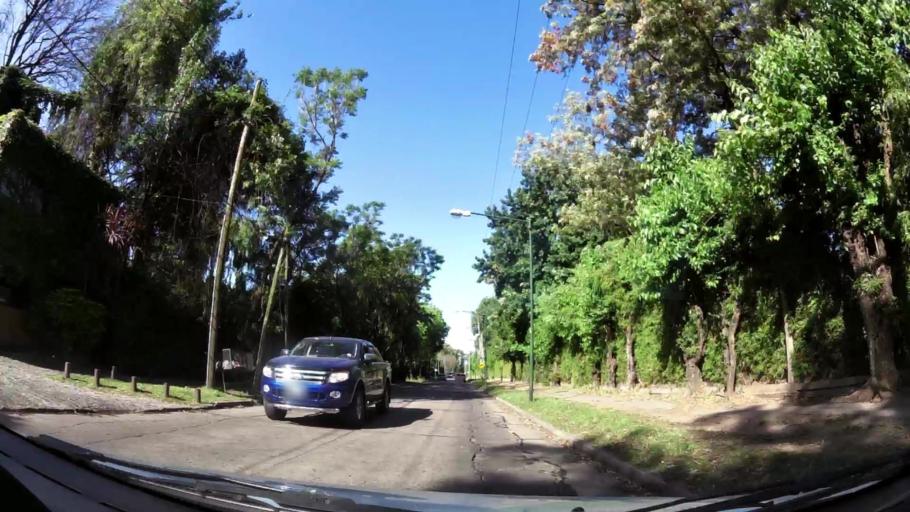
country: AR
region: Buenos Aires
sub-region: Partido de San Isidro
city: San Isidro
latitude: -34.4866
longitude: -58.5533
